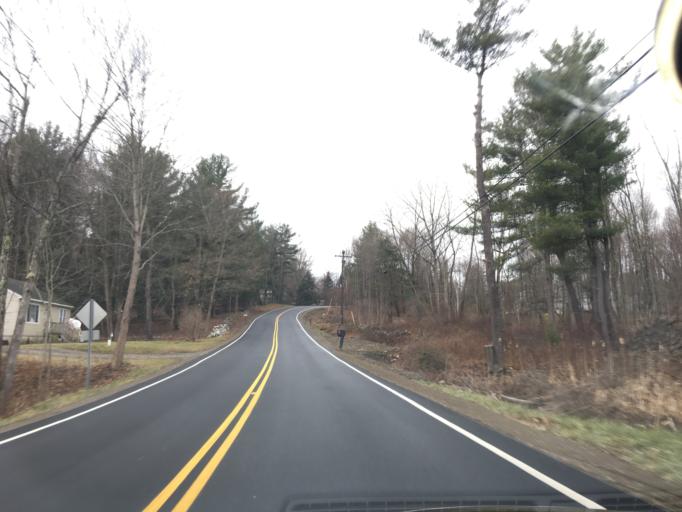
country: US
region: New York
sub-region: Rensselaer County
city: Averill Park
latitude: 42.6155
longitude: -73.5757
